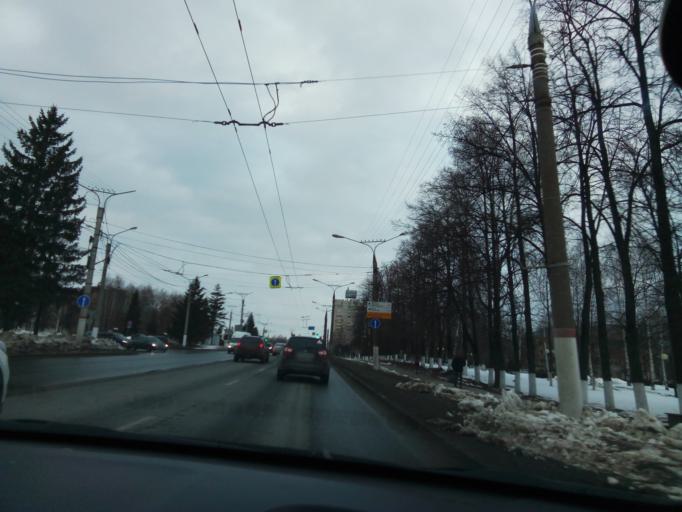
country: RU
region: Chuvashia
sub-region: Cheboksarskiy Rayon
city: Cheboksary
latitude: 56.1463
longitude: 47.2244
